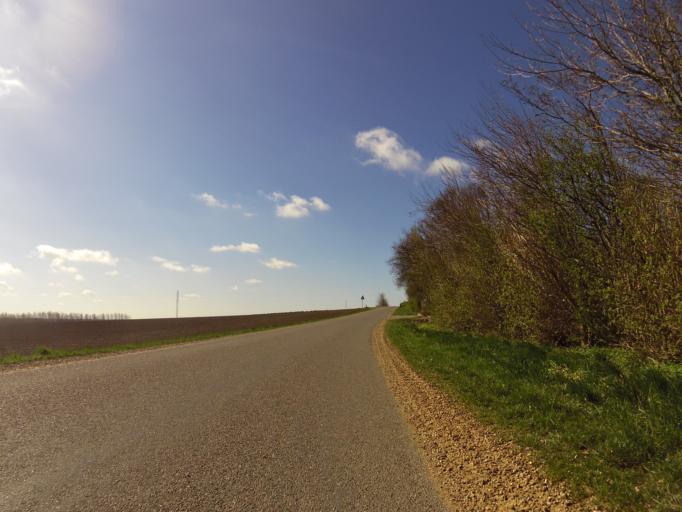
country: DK
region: Central Jutland
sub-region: Holstebro Kommune
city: Vinderup
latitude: 56.4490
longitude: 8.7229
